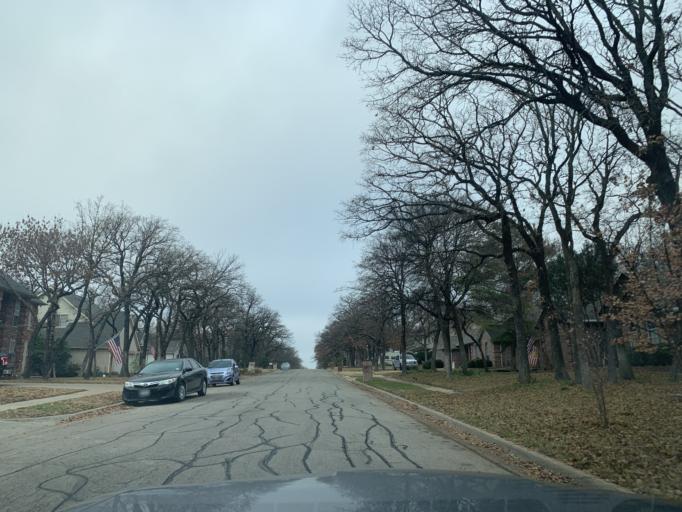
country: US
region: Texas
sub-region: Tarrant County
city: Bedford
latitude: 32.8336
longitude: -97.1464
